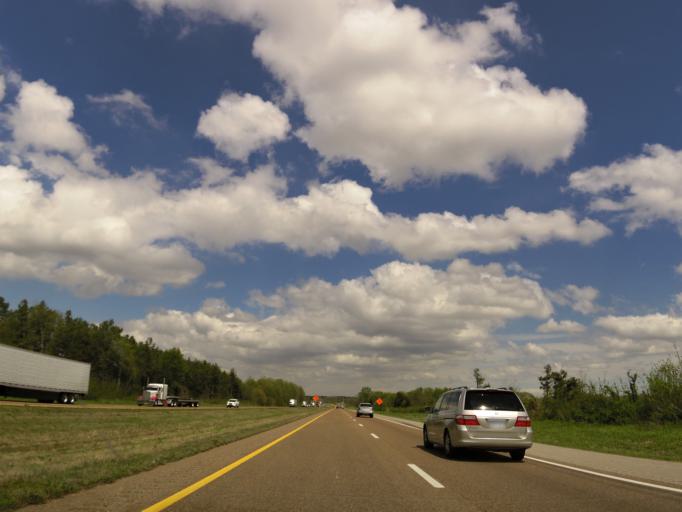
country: US
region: Tennessee
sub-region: Shelby County
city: Arlington
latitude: 35.2824
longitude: -89.6262
